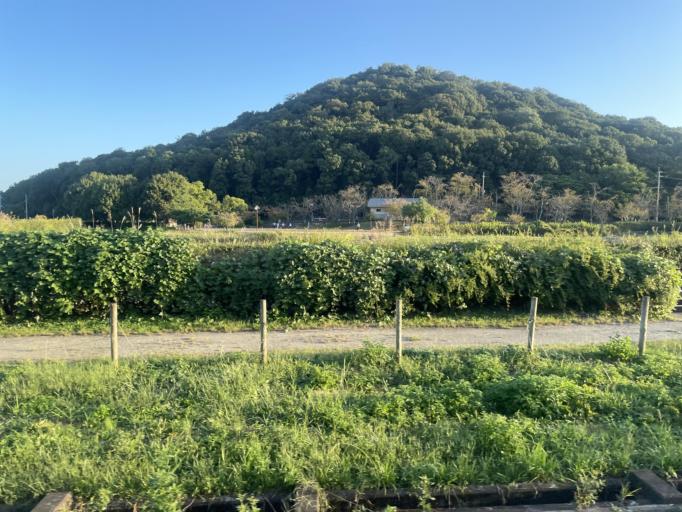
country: JP
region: Nara
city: Kashihara-shi
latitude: 34.5121
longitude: 135.8041
